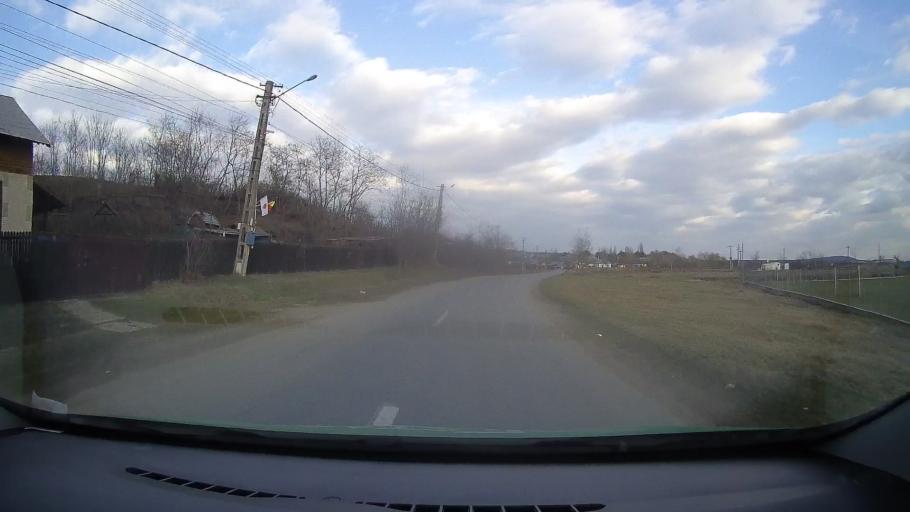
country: RO
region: Dambovita
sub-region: Comuna Gura Ocnitei
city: Gura Ocnitei
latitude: 44.9388
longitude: 25.5732
